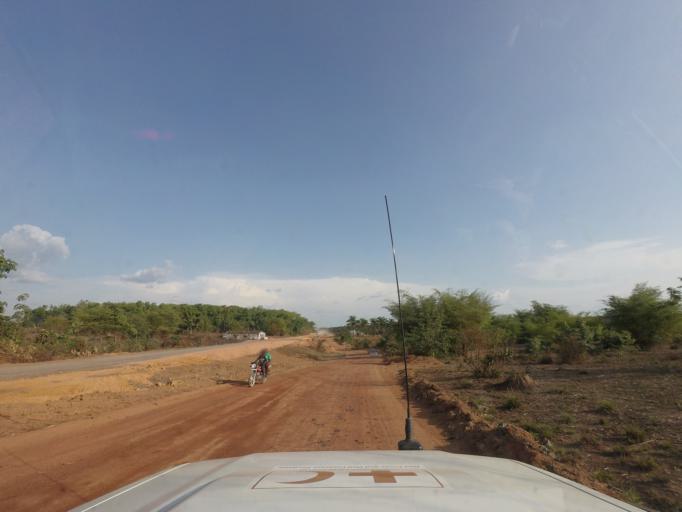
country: LR
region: Bong
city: Gbarnga
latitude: 7.0387
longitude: -9.5136
